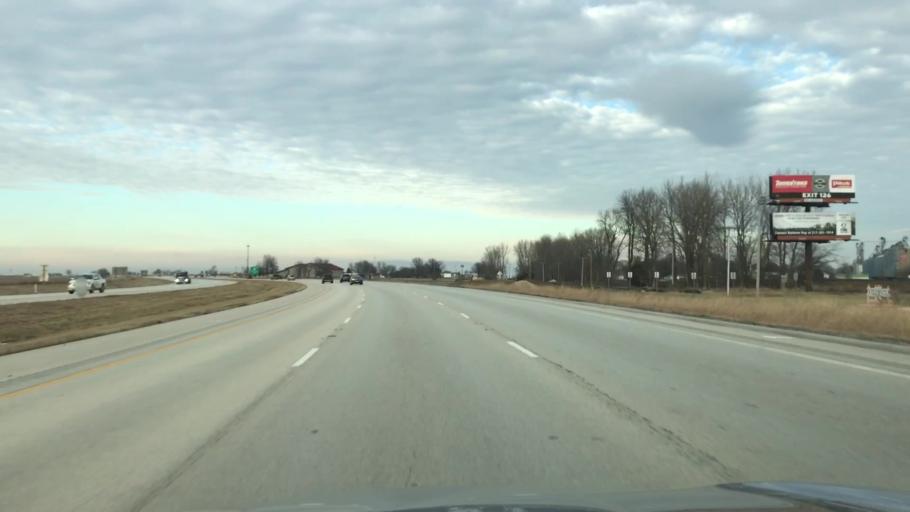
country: US
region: Illinois
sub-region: Sangamon County
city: Williamsville
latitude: 39.9466
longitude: -89.5576
